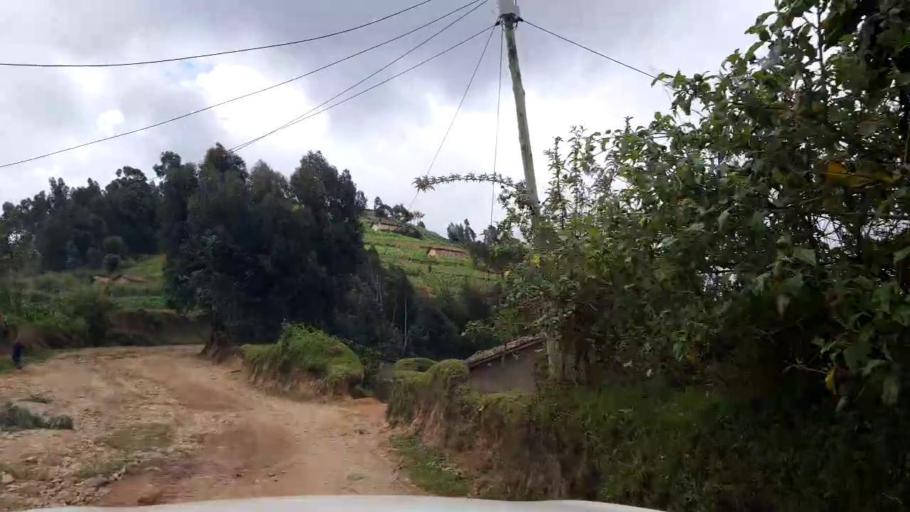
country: RW
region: Western Province
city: Kibuye
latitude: -1.8975
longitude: 29.4555
